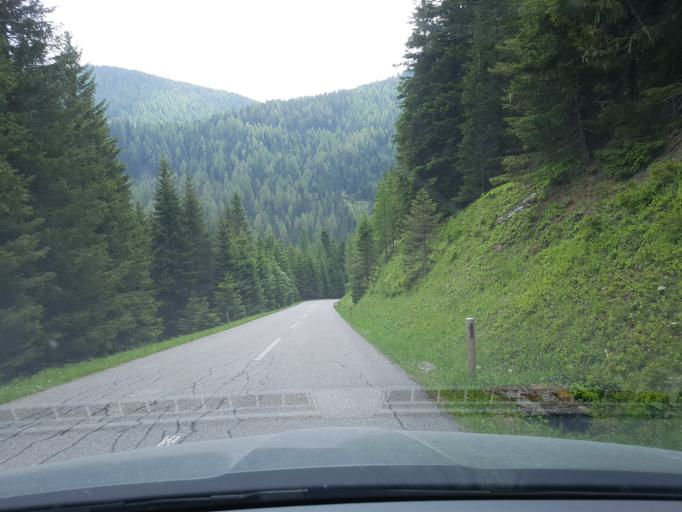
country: AT
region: Carinthia
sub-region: Politischer Bezirk Spittal an der Drau
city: Kleinkirchheim
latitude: 46.8923
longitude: 13.8218
